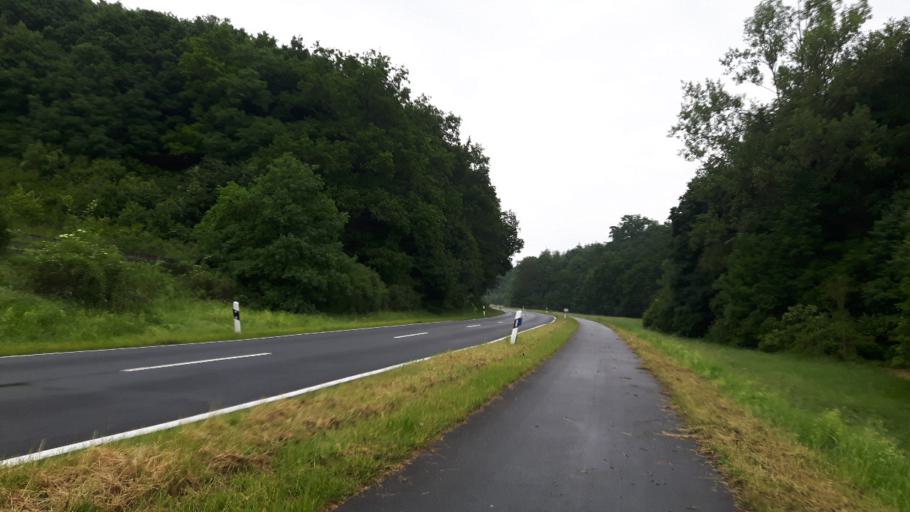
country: DE
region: Bavaria
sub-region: Regierungsbezirk Unterfranken
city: Uchtelhausen
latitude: 50.1173
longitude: 10.2741
